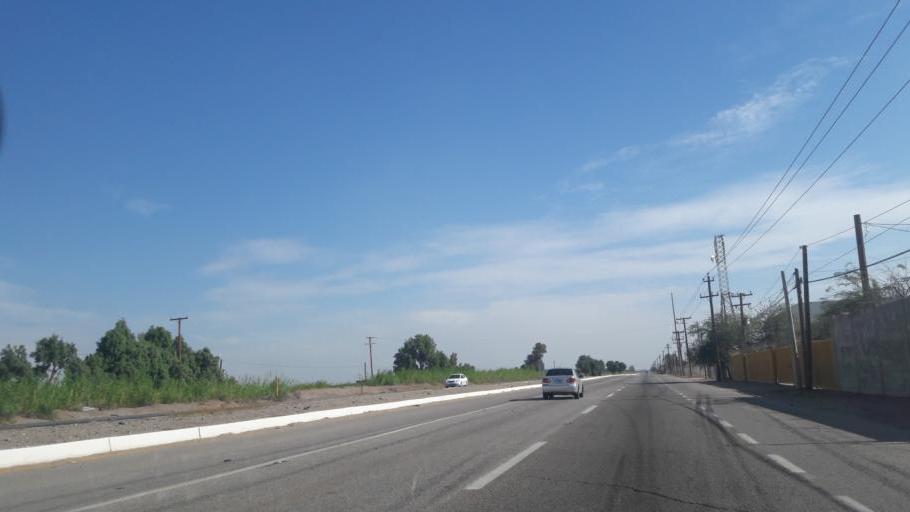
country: MX
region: Baja California
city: Progreso
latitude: 32.5945
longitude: -115.6295
